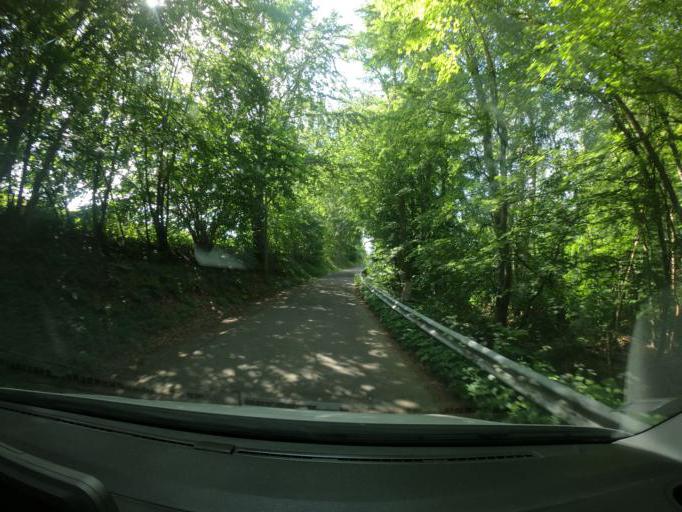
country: SE
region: Skane
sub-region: Bastads Kommun
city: Bastad
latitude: 56.4106
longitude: 12.8649
